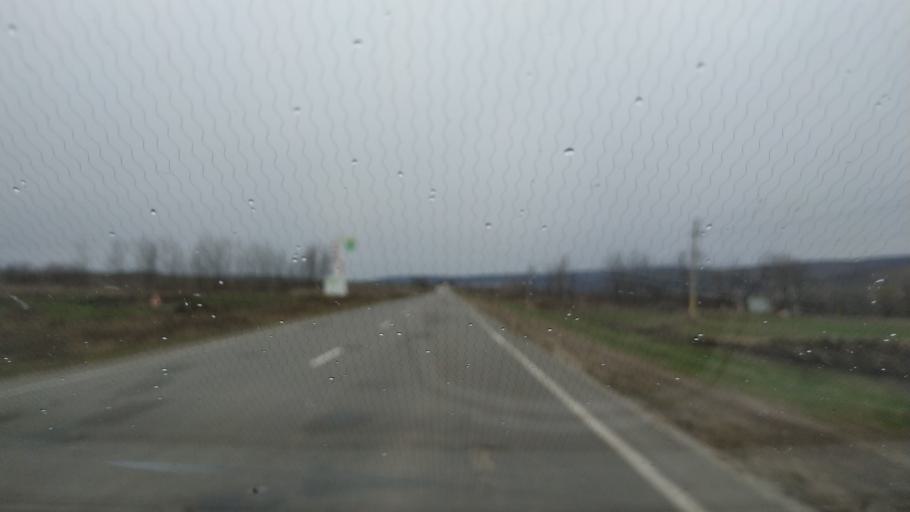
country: MD
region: Hincesti
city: Hincesti
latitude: 46.7585
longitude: 28.5224
